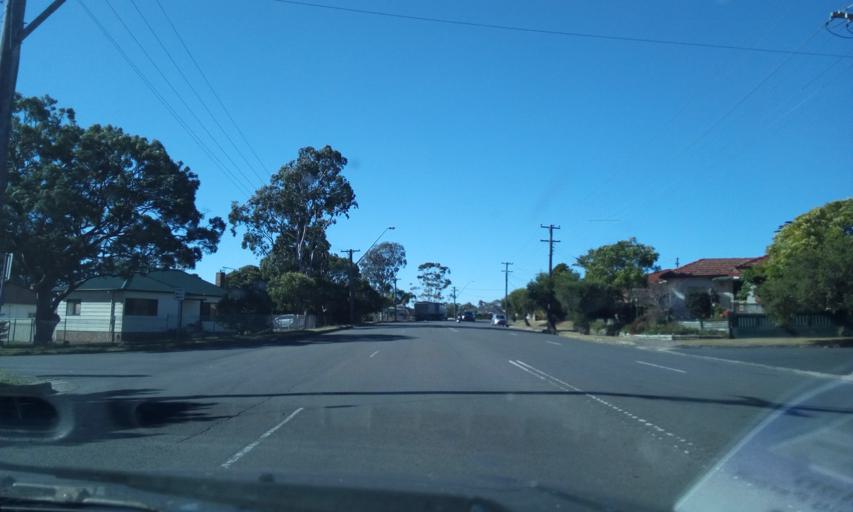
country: AU
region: New South Wales
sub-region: Wollongong
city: Dapto
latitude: -34.4984
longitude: 150.7923
